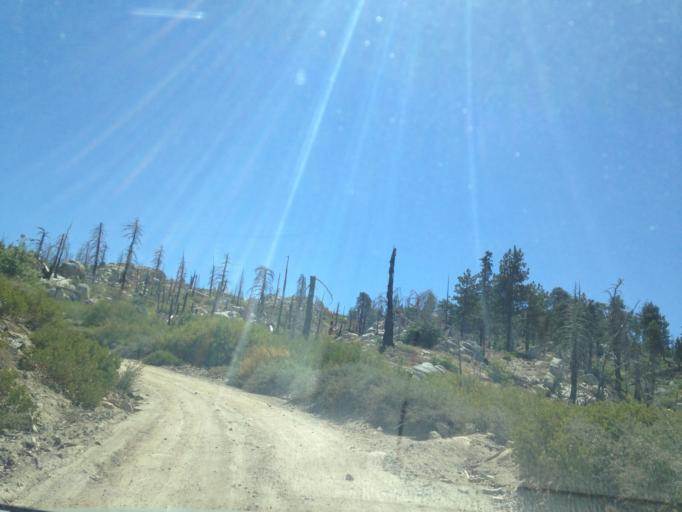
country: US
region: California
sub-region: San Bernardino County
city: Big Bear Lake
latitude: 34.2638
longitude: -116.9916
